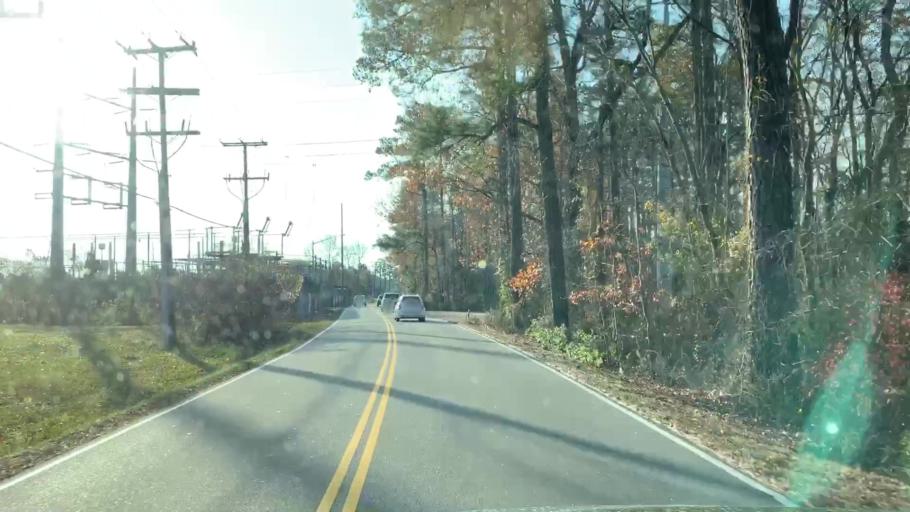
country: US
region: Virginia
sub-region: City of Chesapeake
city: Chesapeake
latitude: 36.7802
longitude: -76.1583
